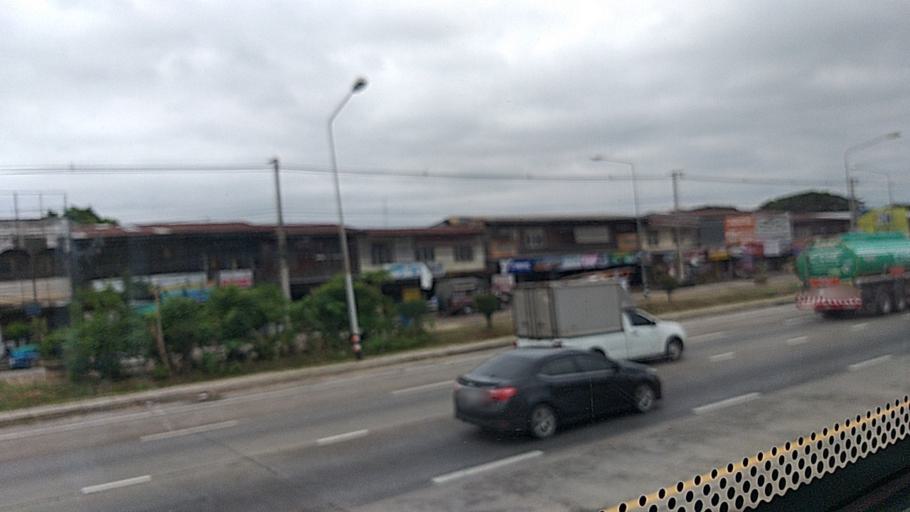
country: TH
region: Khon Kaen
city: Phon
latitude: 15.8131
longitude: 102.6076
